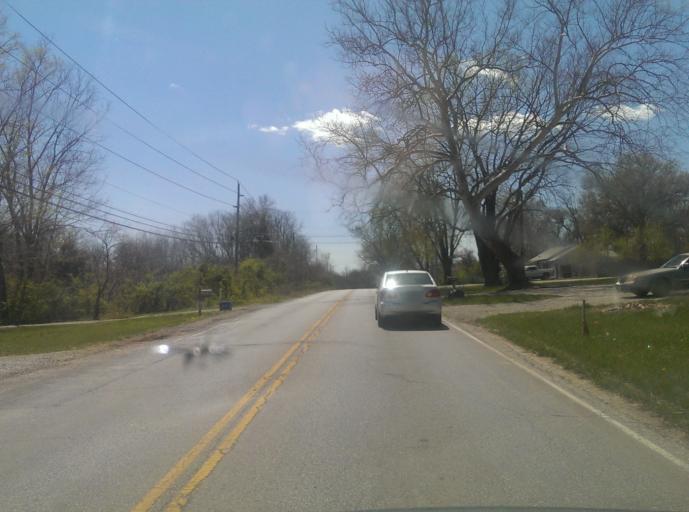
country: US
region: Missouri
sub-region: Jackson County
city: Grandview
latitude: 38.8989
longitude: -94.5854
